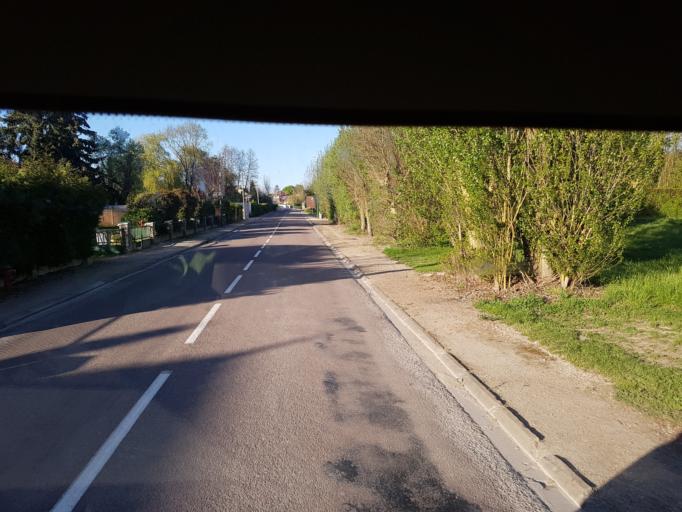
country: FR
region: Champagne-Ardenne
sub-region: Departement de l'Aube
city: Marigny-le-Chatel
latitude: 48.4374
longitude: 3.6773
